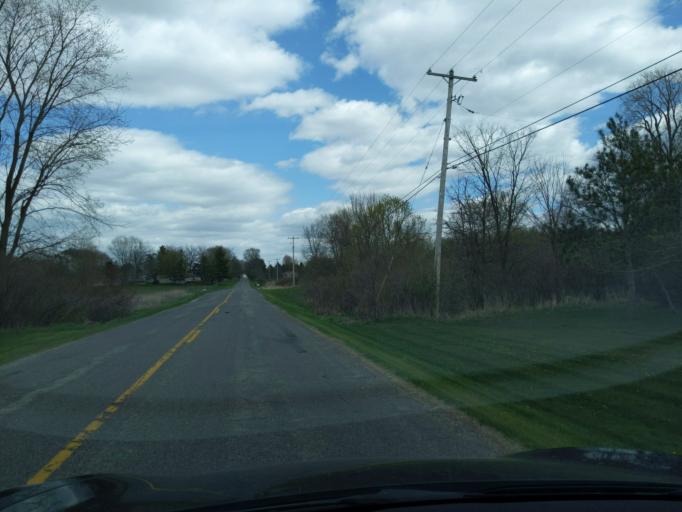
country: US
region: Michigan
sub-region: Ingham County
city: Holt
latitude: 42.6185
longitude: -84.5322
